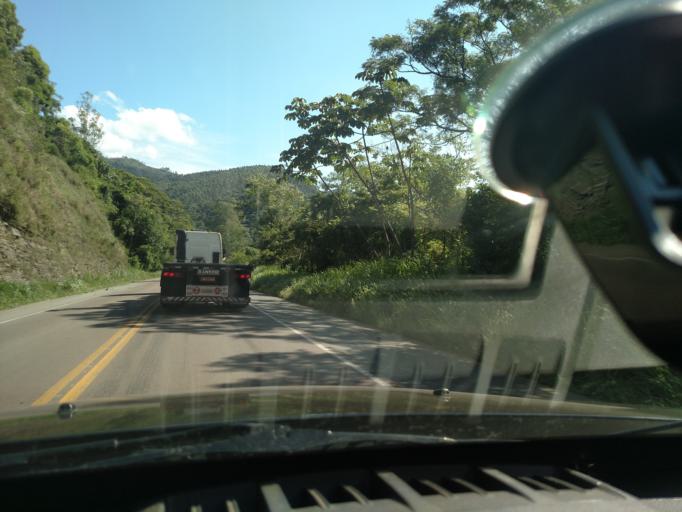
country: BR
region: Santa Catarina
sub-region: Ibirama
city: Ibirama
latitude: -27.0697
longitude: -49.4198
